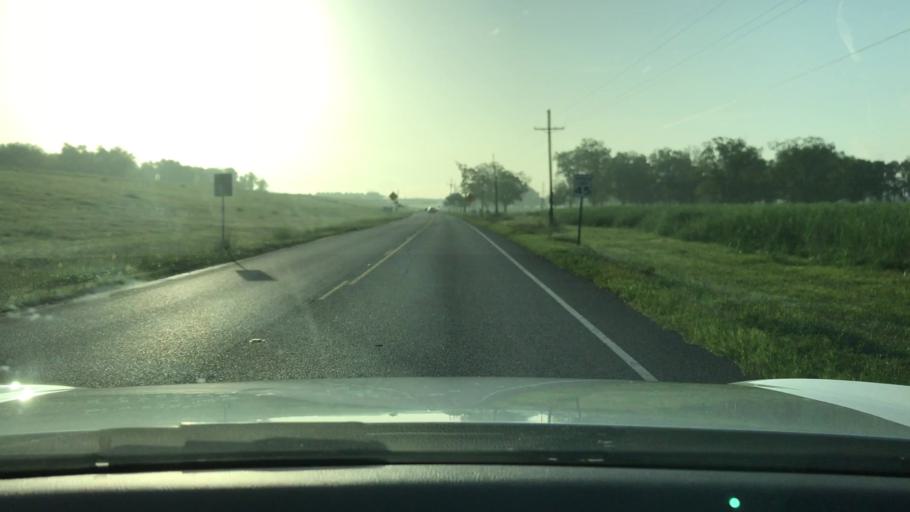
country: US
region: Louisiana
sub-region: Iberville Parish
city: Plaquemine
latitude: 30.2727
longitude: -91.1901
